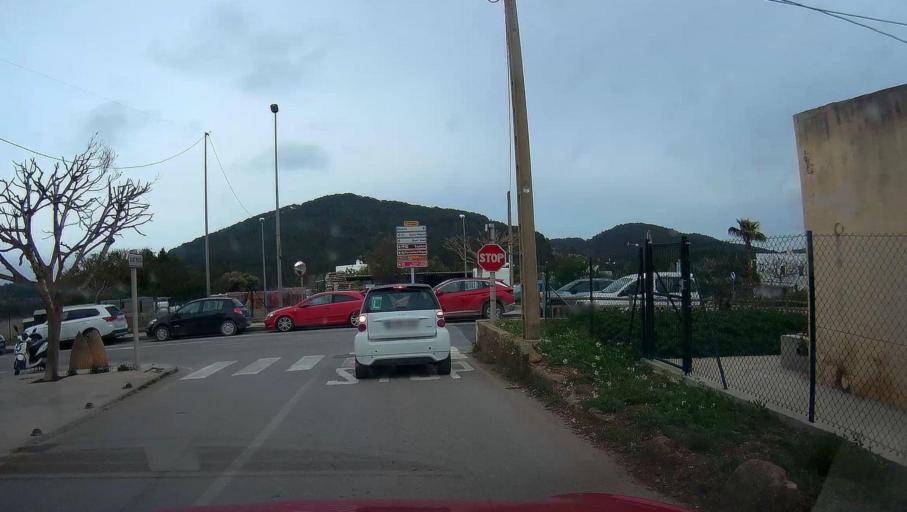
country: ES
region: Balearic Islands
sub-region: Illes Balears
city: Sant Joan de Labritja
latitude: 39.0530
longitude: 1.4366
